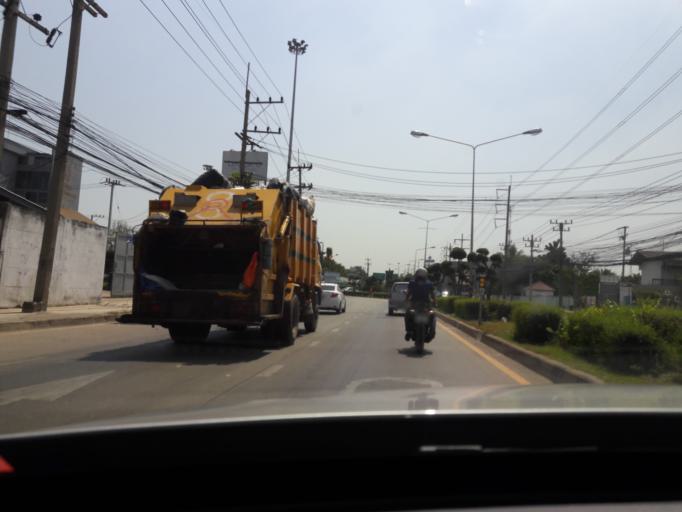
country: TH
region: Samut Sakhon
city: Samut Sakhon
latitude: 13.5633
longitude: 100.2721
